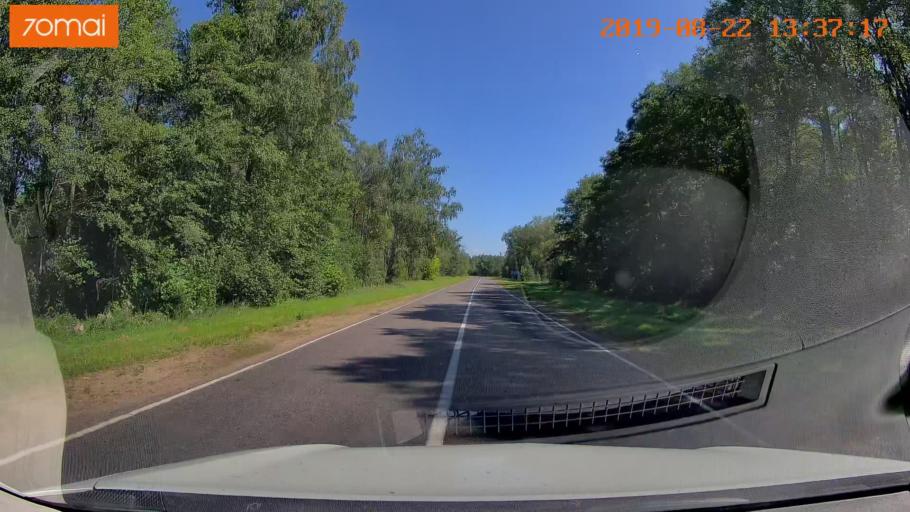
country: BY
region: Minsk
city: Staryya Darohi
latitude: 53.2172
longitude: 28.2957
